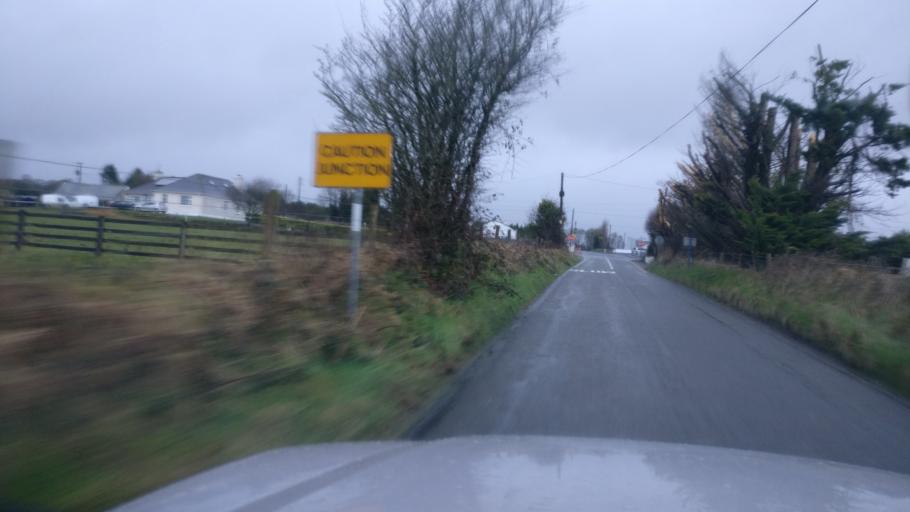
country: IE
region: Connaught
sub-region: County Galway
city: Loughrea
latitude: 53.2678
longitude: -8.4078
